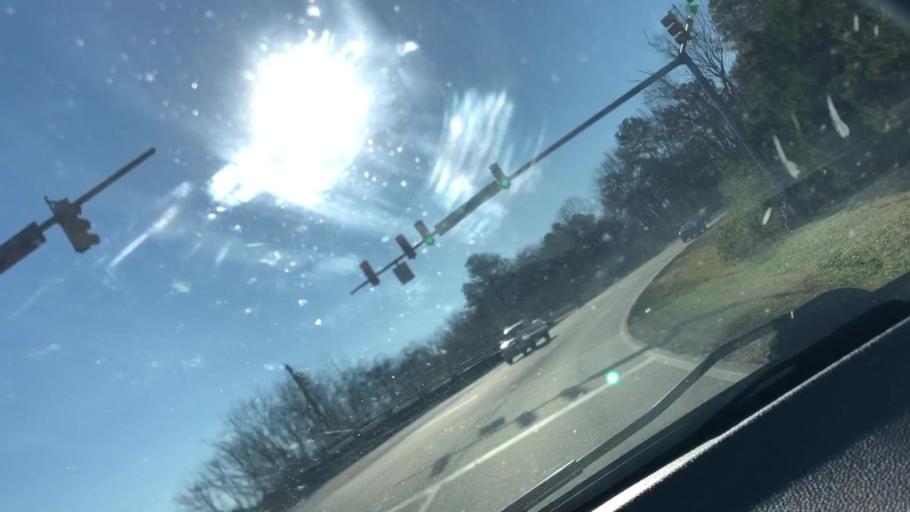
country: US
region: Georgia
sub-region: Bartow County
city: Cartersville
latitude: 34.2208
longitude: -84.8020
